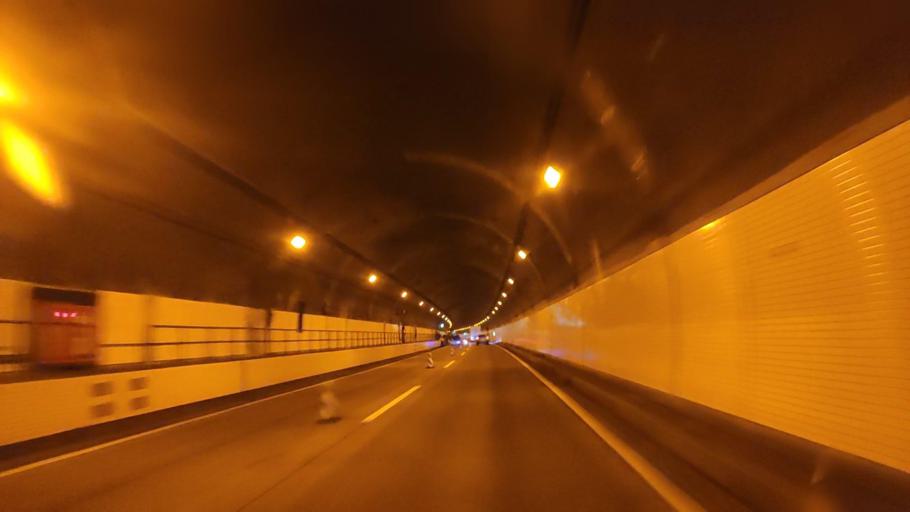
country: JP
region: Niigata
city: Joetsu
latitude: 37.1052
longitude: 138.0397
